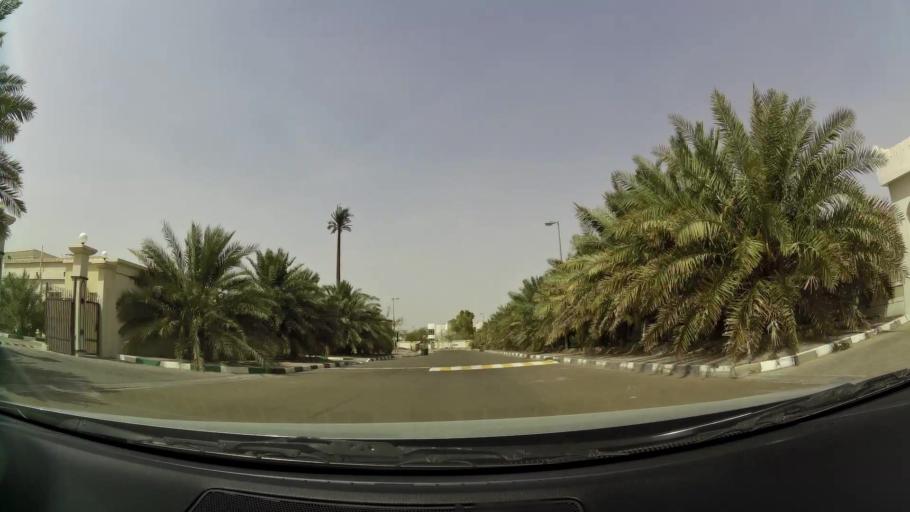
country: AE
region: Abu Dhabi
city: Al Ain
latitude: 24.1573
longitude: 55.6542
